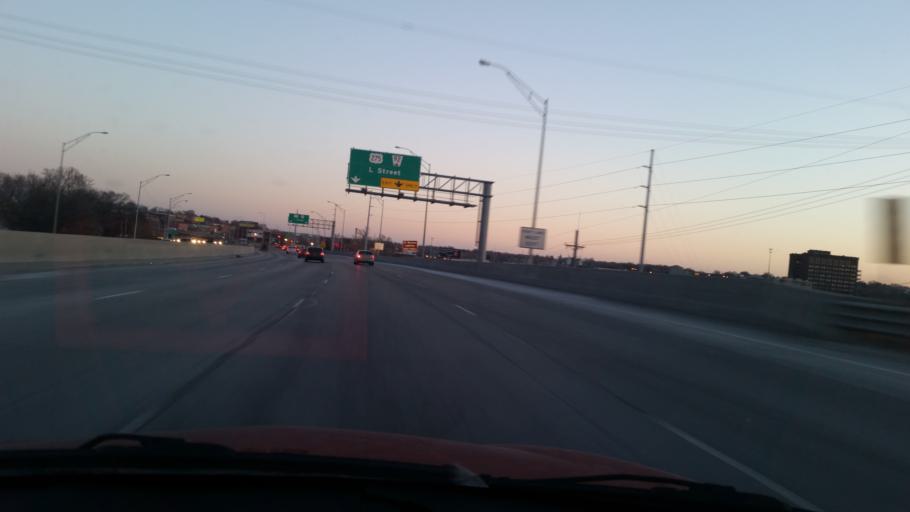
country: US
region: Nebraska
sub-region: Douglas County
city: Omaha
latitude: 41.2162
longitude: -95.9534
